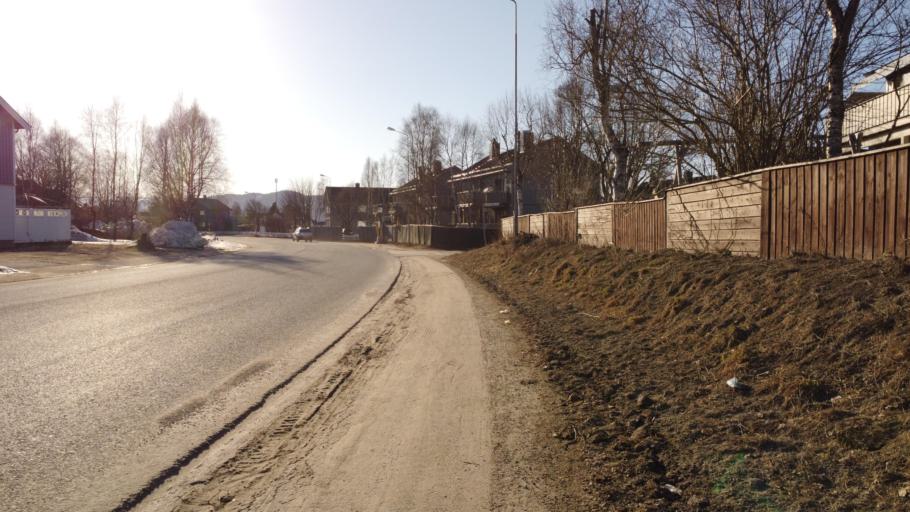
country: NO
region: Nordland
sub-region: Rana
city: Mo i Rana
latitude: 66.3196
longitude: 14.1880
